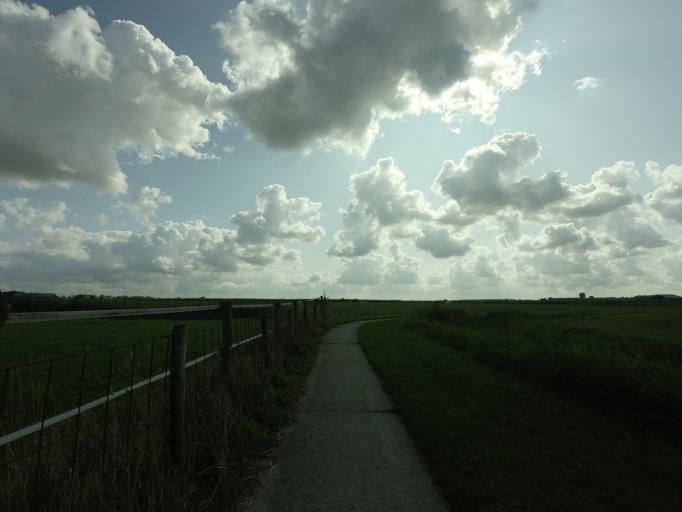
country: NL
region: Friesland
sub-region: Gemeente Het Bildt
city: Sint Jacobiparochie
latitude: 53.2688
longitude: 5.6089
